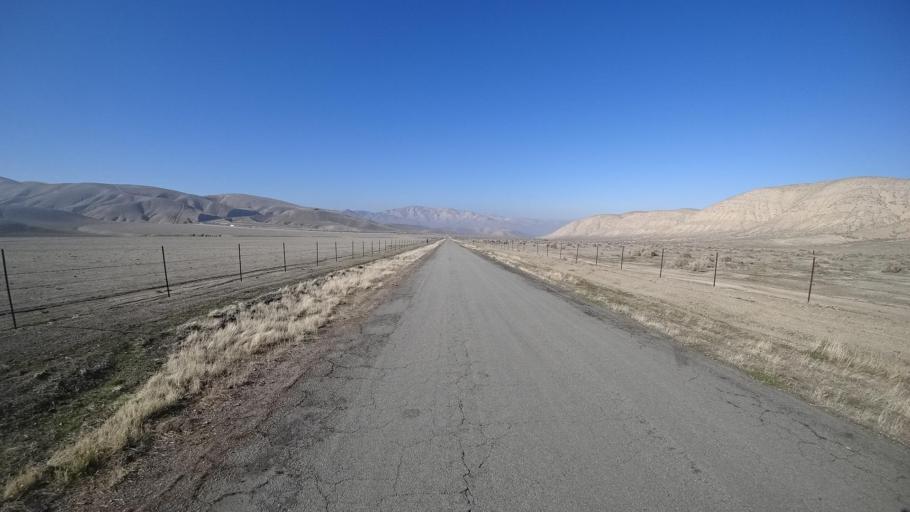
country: US
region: California
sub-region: Kern County
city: Maricopa
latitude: 34.9991
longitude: -119.4006
